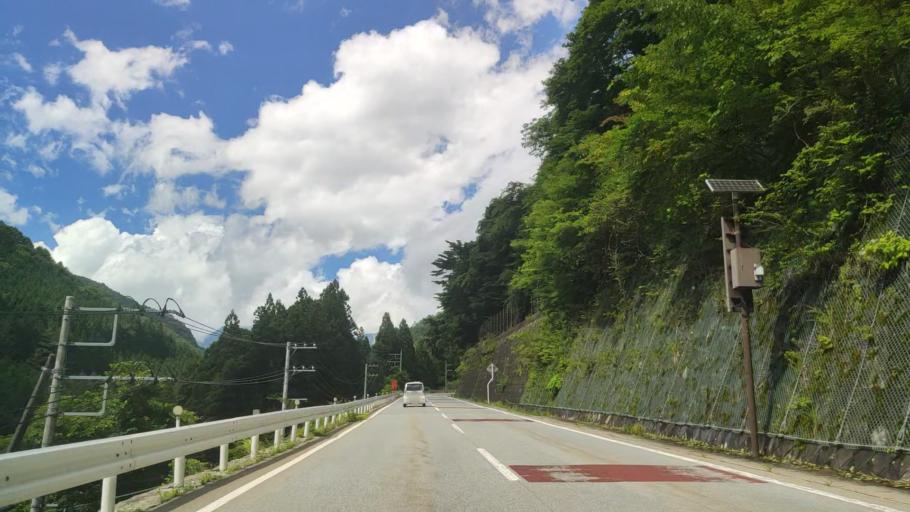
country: JP
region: Yamanashi
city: Enzan
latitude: 35.8257
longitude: 138.7634
